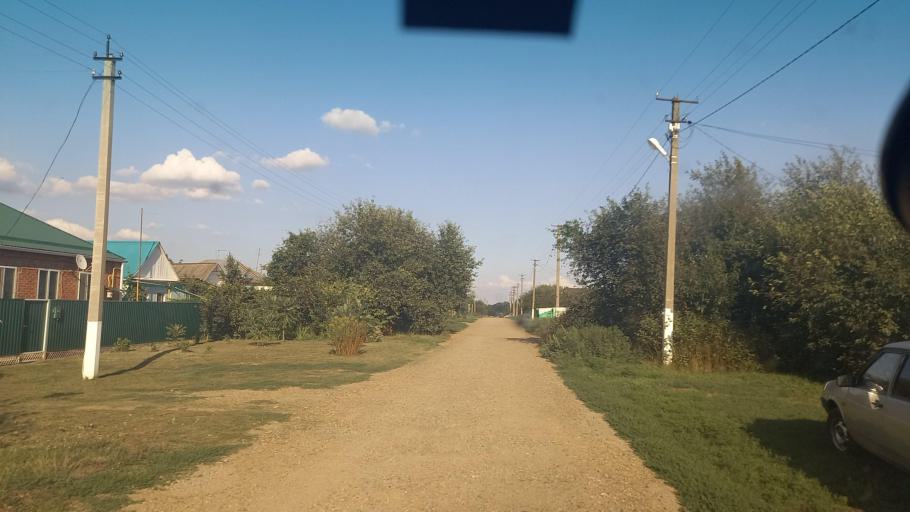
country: RU
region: Adygeya
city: Khatukay
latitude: 45.2974
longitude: 39.5661
